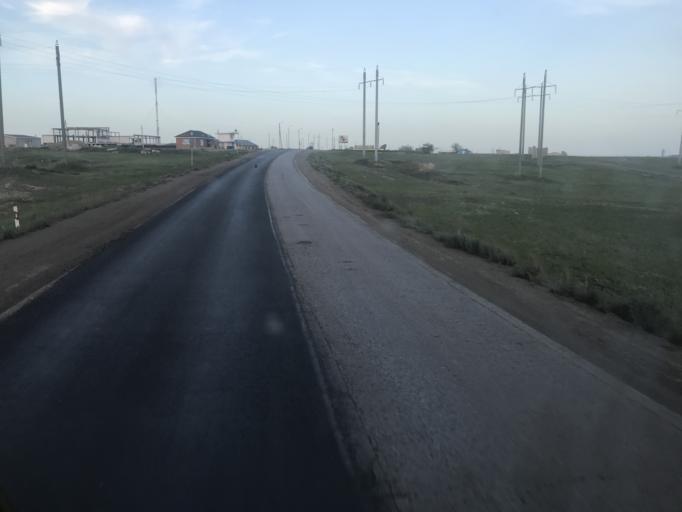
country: KZ
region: Aqtoebe
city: Khromtau
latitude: 50.2590
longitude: 58.4075
